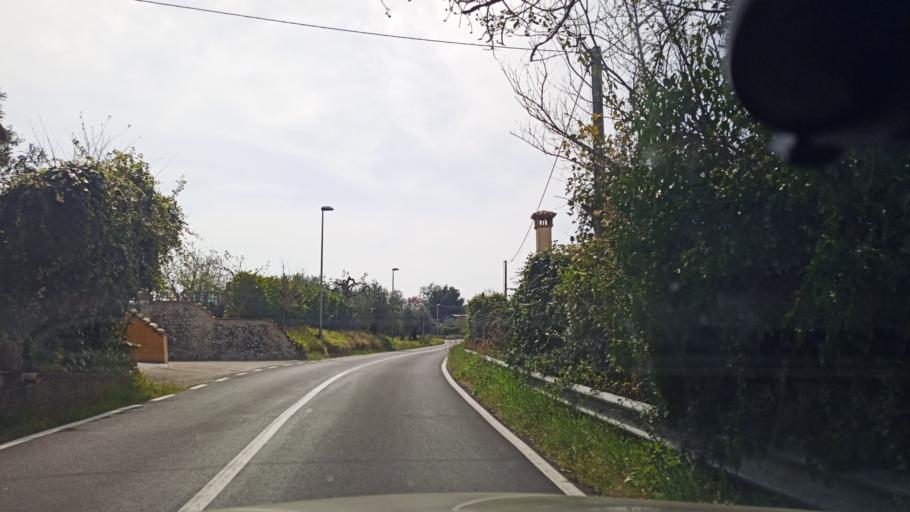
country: IT
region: Latium
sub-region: Provincia di Rieti
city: Torri in Sabina
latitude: 42.3413
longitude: 12.6516
